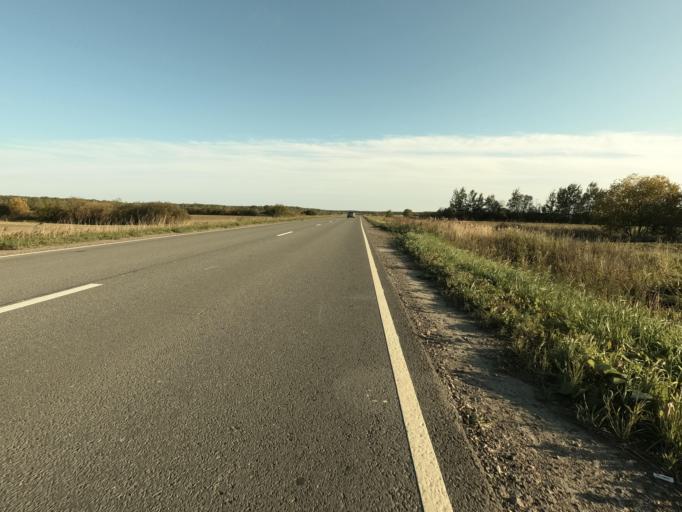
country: RU
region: St.-Petersburg
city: Sapernyy
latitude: 59.7440
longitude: 30.6470
